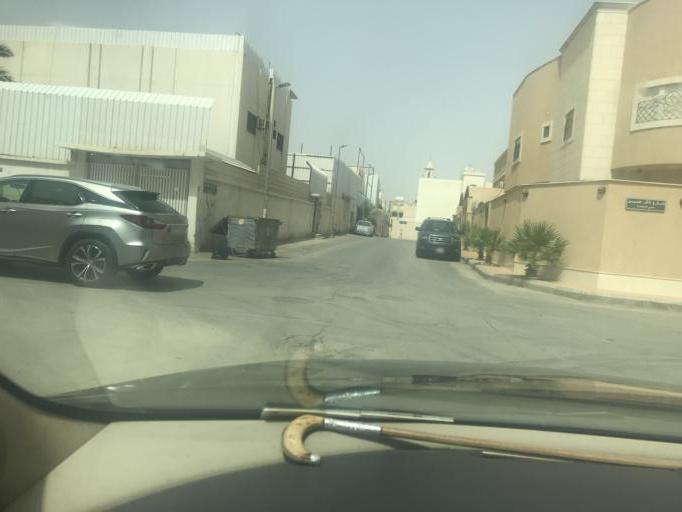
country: SA
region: Ar Riyad
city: Riyadh
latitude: 24.7447
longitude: 46.7697
